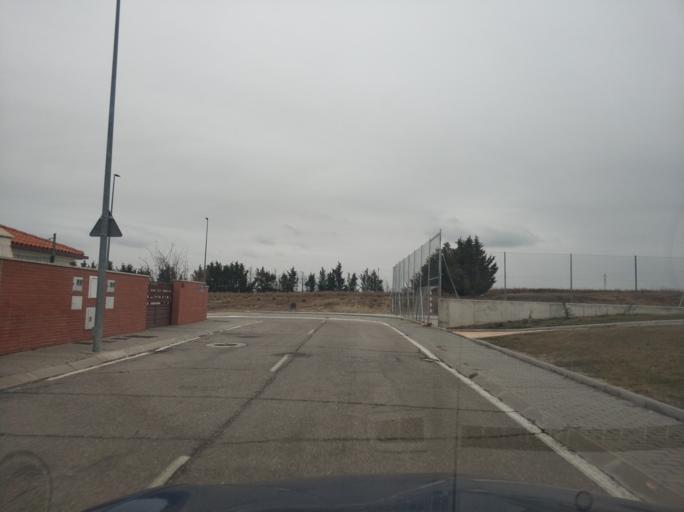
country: ES
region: Castille and Leon
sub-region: Provincia de Salamanca
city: Castellanos de Moriscos
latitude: 41.0111
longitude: -5.6050
